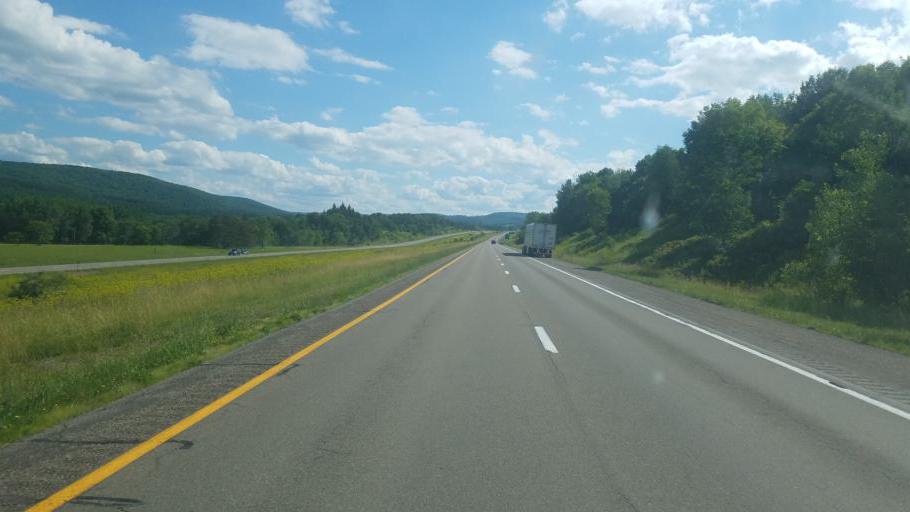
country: US
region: New York
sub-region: Steuben County
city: Hornell
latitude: 42.3429
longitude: -77.7265
